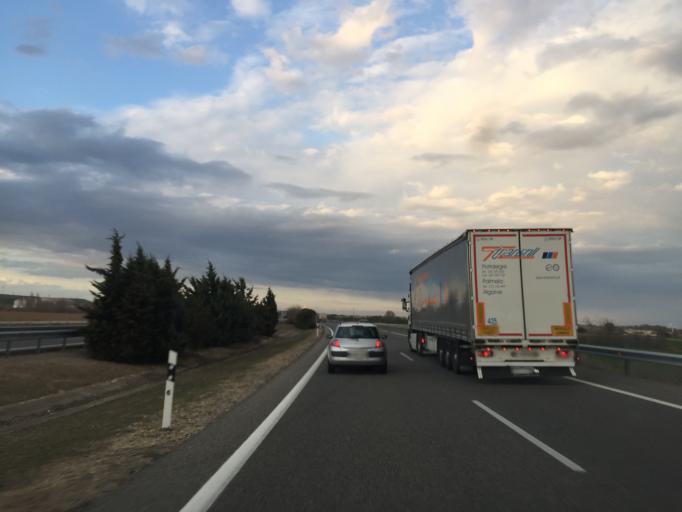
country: ES
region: Castille and Leon
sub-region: Provincia de Palencia
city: Villodrigo
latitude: 42.1408
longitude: -4.1066
